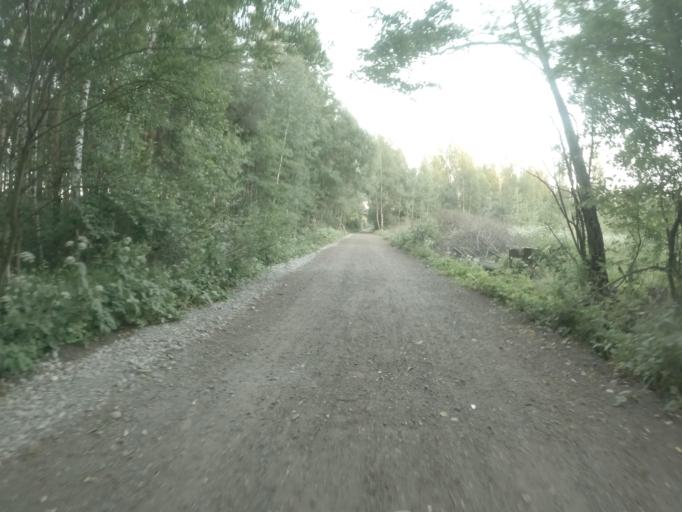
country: RU
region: St.-Petersburg
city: Krasnogvargeisky
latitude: 59.9545
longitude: 30.5041
